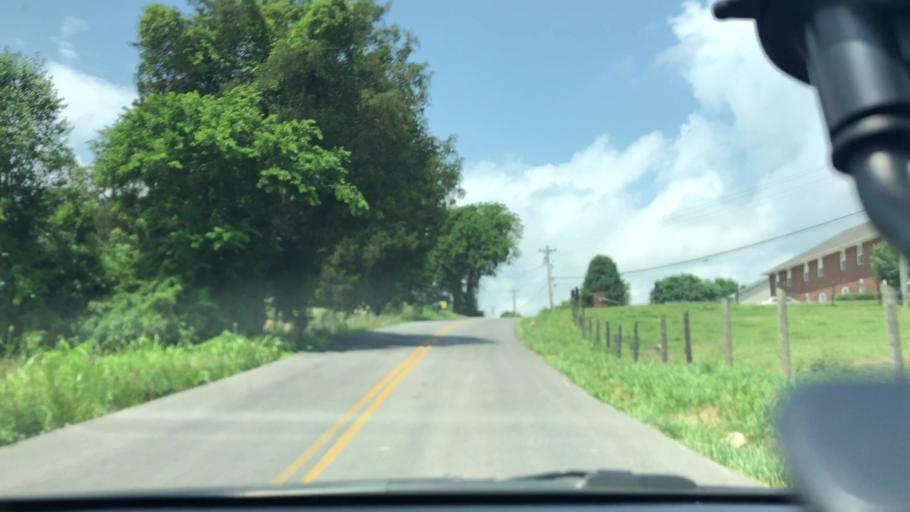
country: US
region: Kentucky
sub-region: Pulaski County
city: Somerset
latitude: 37.0594
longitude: -84.6651
